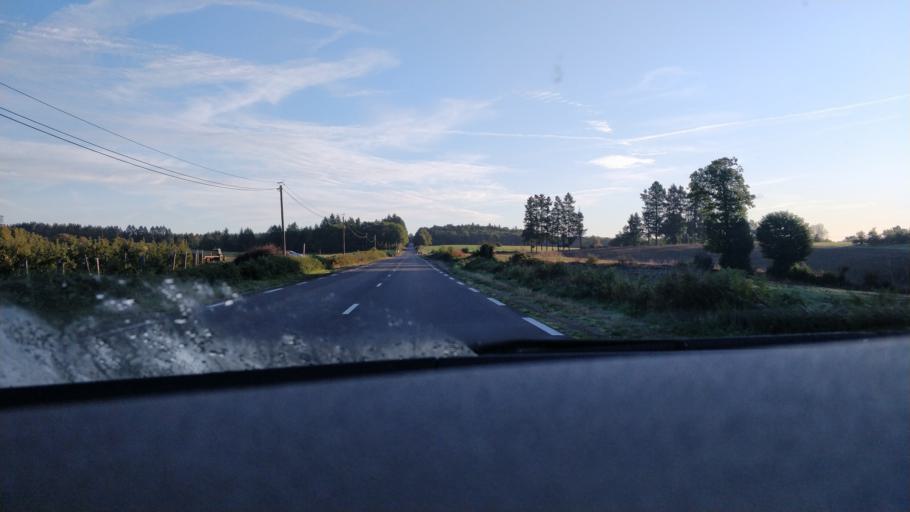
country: FR
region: Limousin
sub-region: Departement de la Haute-Vienne
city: Saint-Leonard-de-Noblat
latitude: 45.8669
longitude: 1.5267
